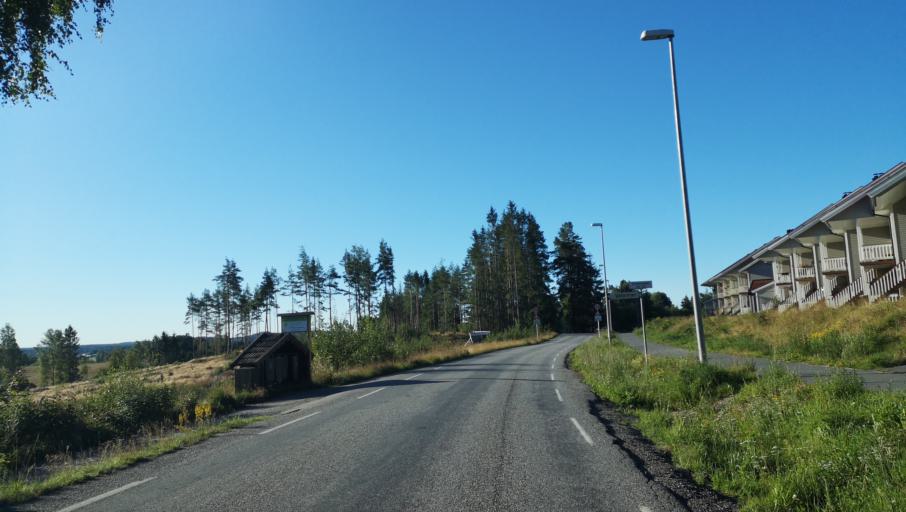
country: NO
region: Ostfold
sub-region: Hobol
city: Knappstad
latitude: 59.6303
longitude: 11.0267
